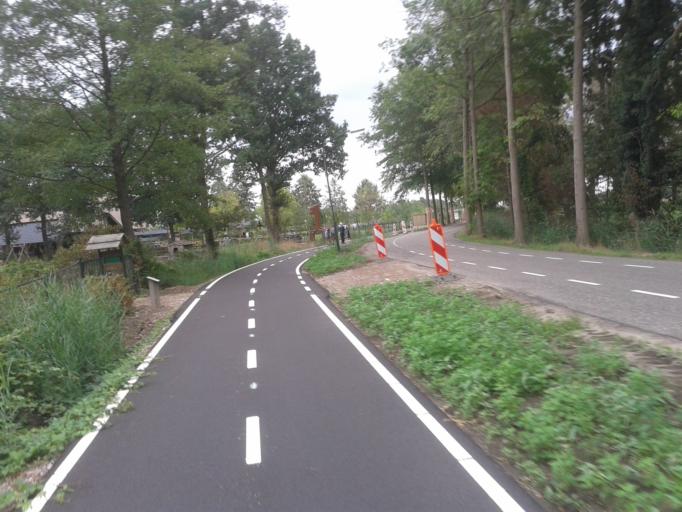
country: NL
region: North Brabant
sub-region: Gemeente Hilvarenbeek
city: Hilvarenbeek
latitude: 51.5193
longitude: 5.1831
